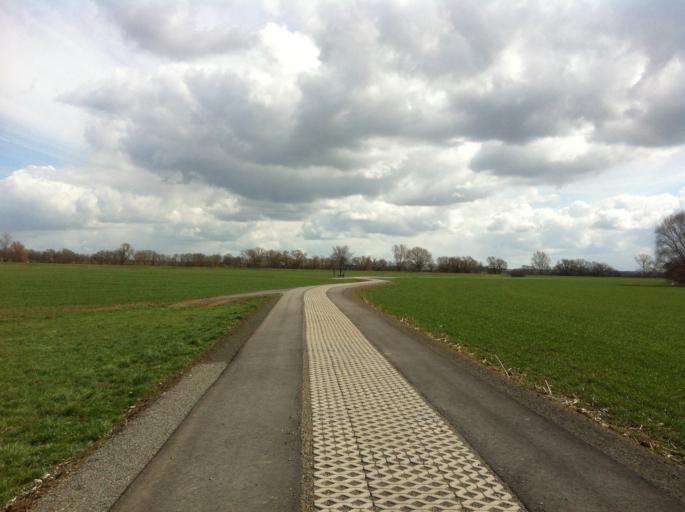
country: DE
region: Saxony
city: Trebsen
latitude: 51.3035
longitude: 12.7474
